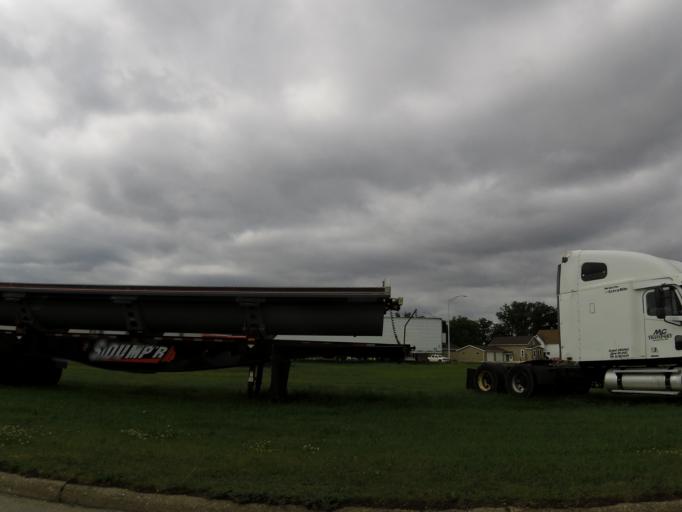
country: US
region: Minnesota
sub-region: Polk County
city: East Grand Forks
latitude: 47.9275
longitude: -97.0161
